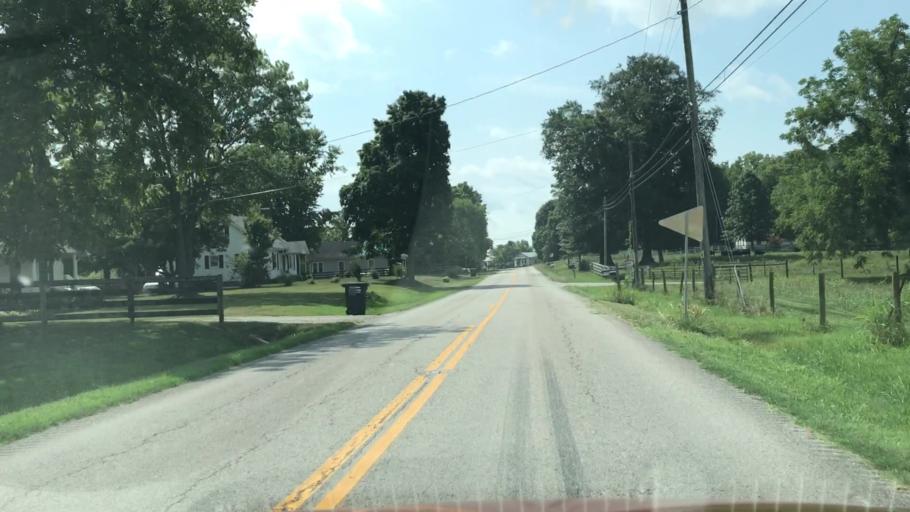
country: US
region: Kentucky
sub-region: Barren County
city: Glasgow
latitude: 36.8920
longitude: -85.8552
